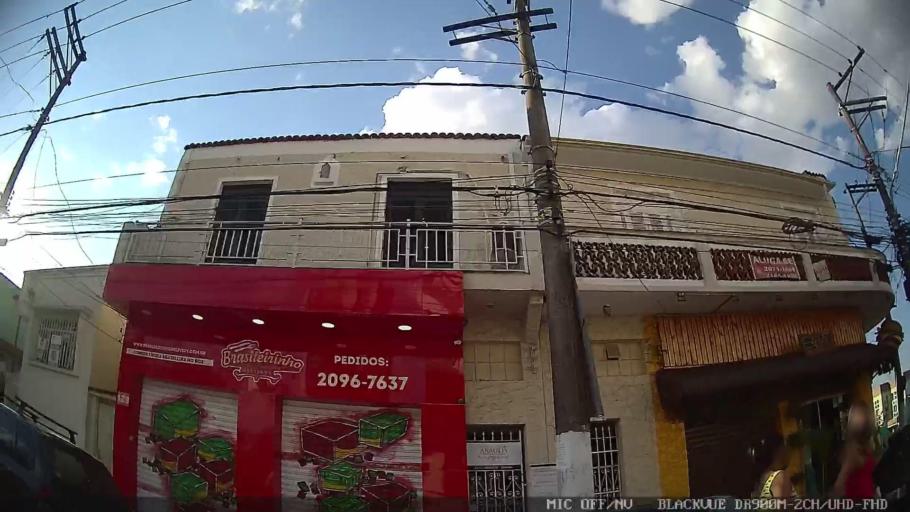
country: BR
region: Sao Paulo
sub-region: Sao Caetano Do Sul
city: Sao Caetano do Sul
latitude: -23.5645
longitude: -46.5447
